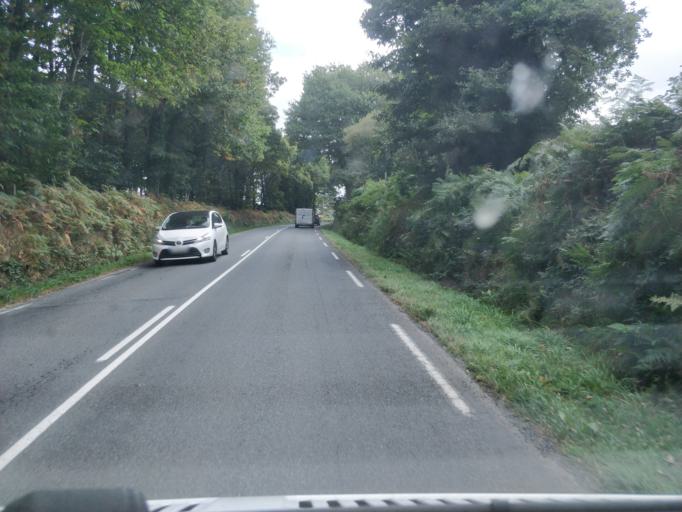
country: FR
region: Brittany
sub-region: Departement du Finistere
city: Pluguffan
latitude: 48.0016
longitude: -4.1801
